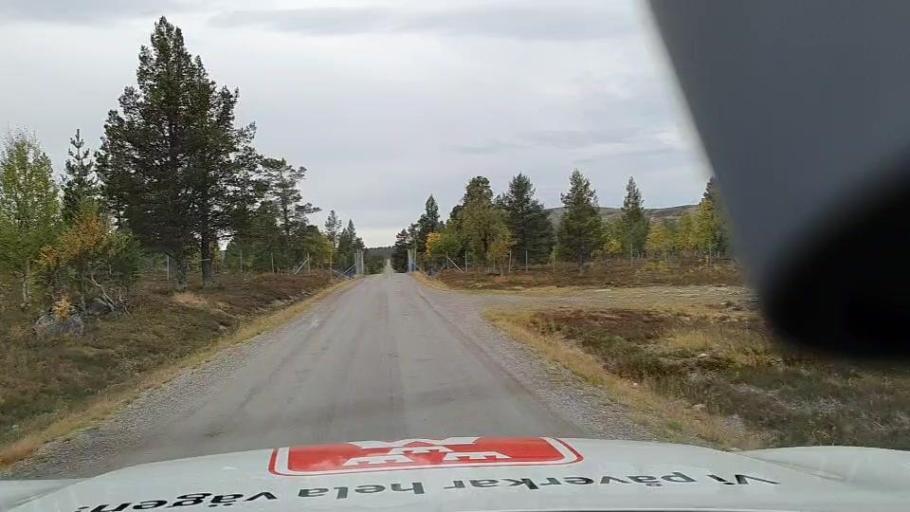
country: NO
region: Hedmark
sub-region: Engerdal
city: Engerdal
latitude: 62.1219
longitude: 12.8679
